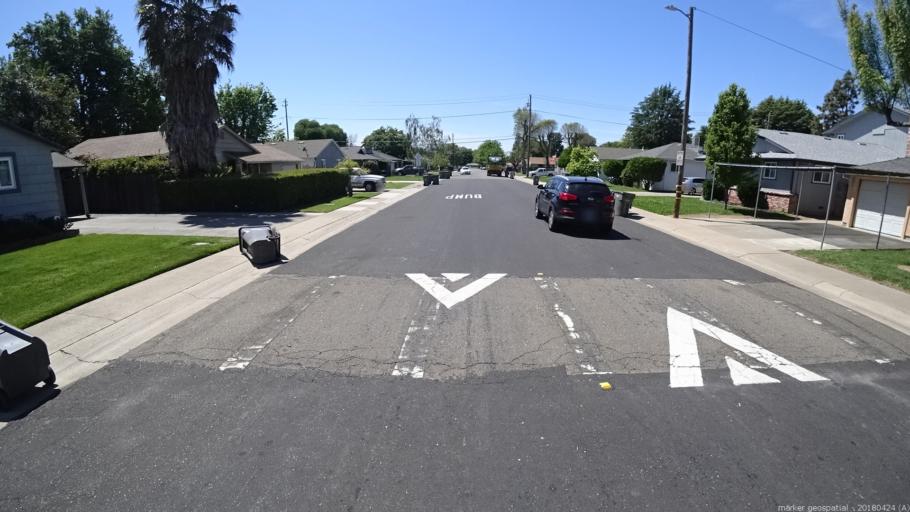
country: US
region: California
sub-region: Yolo County
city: West Sacramento
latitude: 38.5823
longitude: -121.5298
